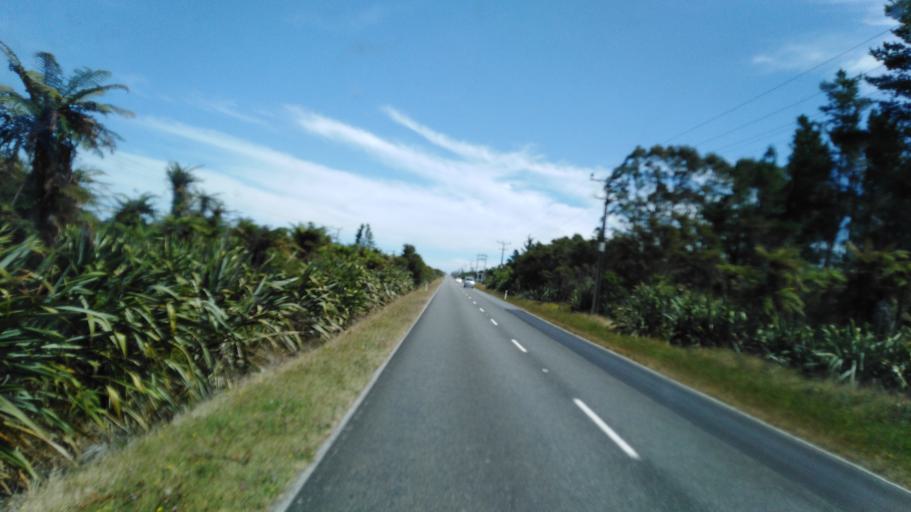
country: NZ
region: West Coast
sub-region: Buller District
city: Westport
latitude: -41.7429
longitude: 171.6914
